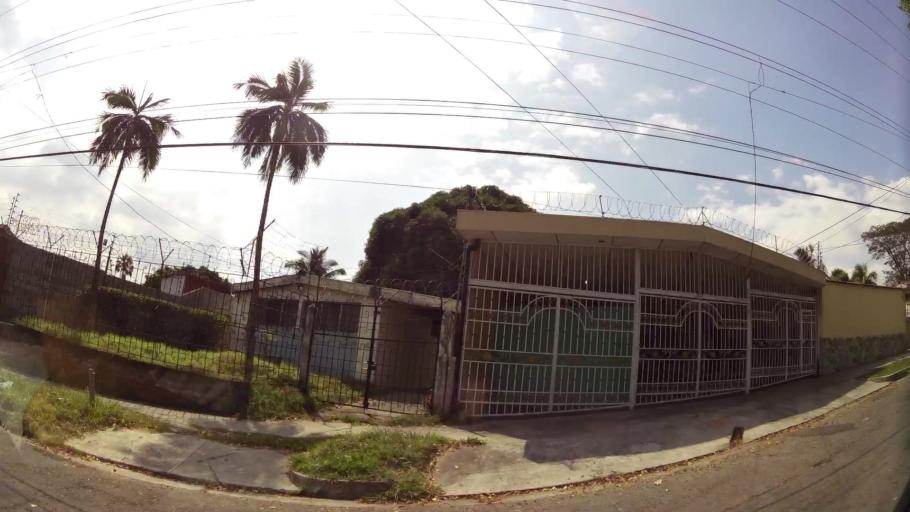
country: SV
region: San Salvador
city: Mejicanos
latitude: 13.7070
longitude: -89.2166
